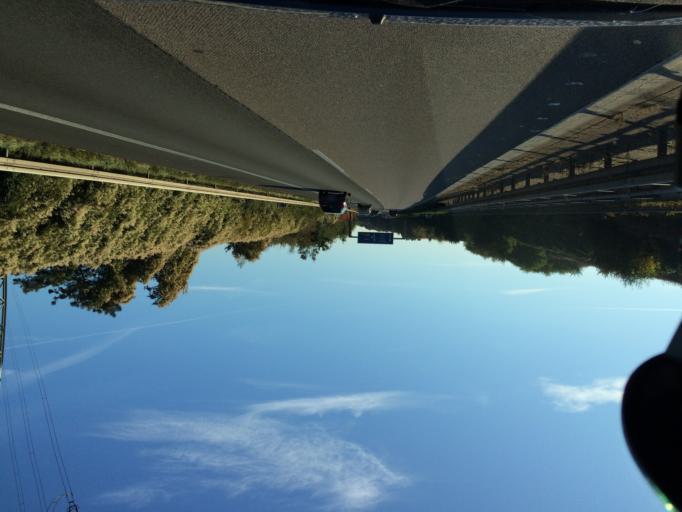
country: DE
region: North Rhine-Westphalia
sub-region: Regierungsbezirk Koln
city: Wahn-Heide
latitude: 50.8513
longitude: 7.0976
